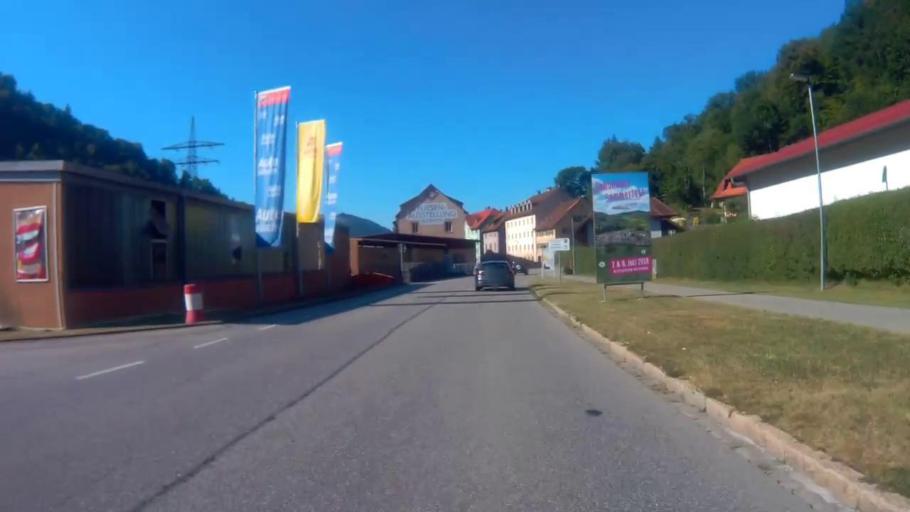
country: DE
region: Baden-Wuerttemberg
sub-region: Freiburg Region
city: Aitern
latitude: 47.7957
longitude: 7.9034
